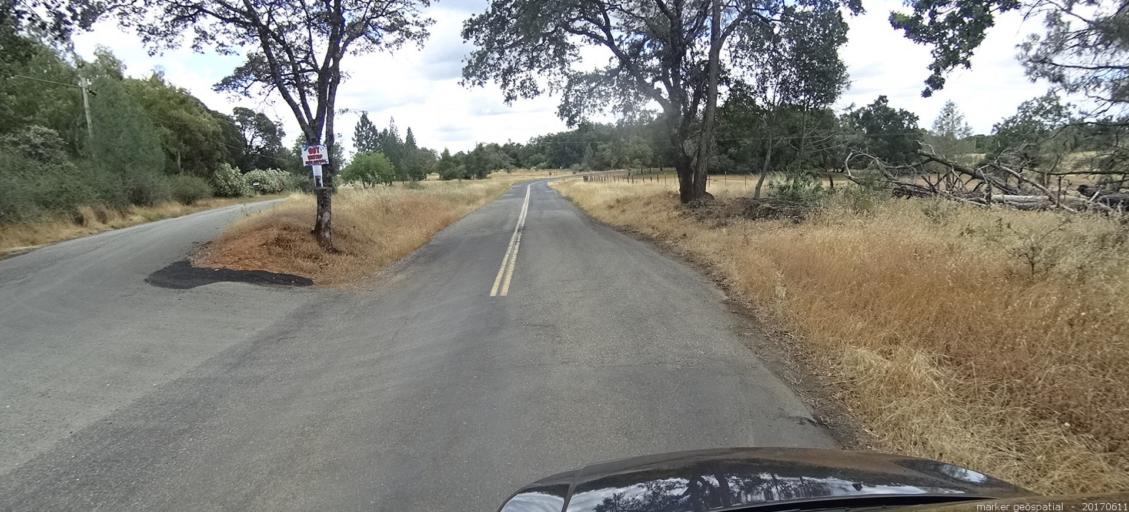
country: US
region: California
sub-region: Butte County
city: Oroville
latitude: 39.6075
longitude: -121.5293
